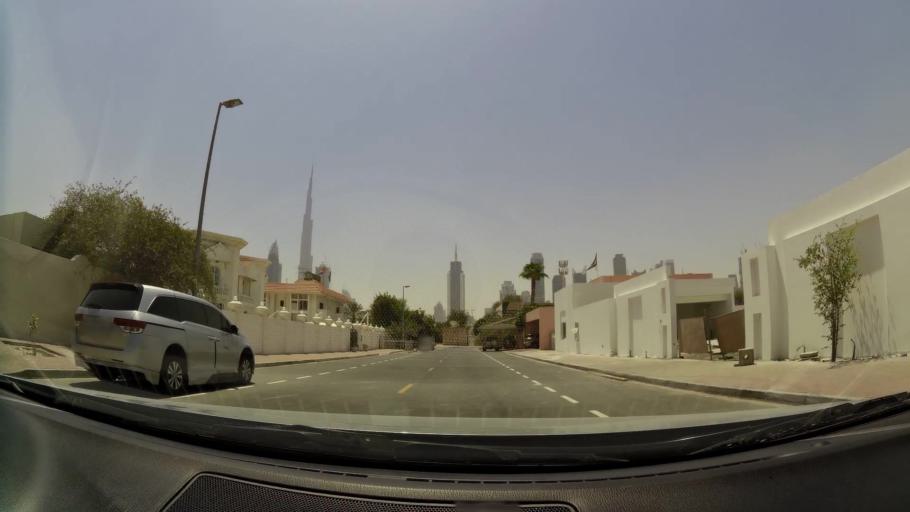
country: AE
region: Dubai
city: Dubai
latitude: 25.2009
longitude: 55.2551
